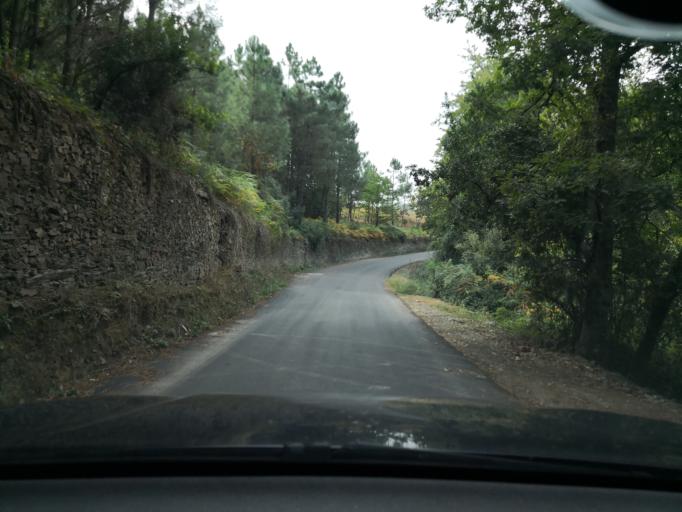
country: PT
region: Vila Real
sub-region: Sabrosa
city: Vilela
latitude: 41.2127
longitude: -7.6852
